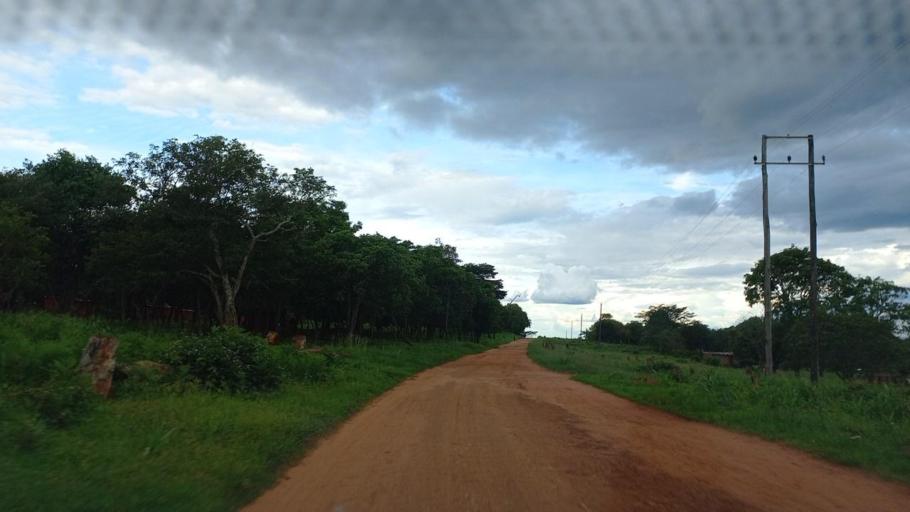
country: ZM
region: North-Western
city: Mwinilunga
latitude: -11.7782
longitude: 24.3780
